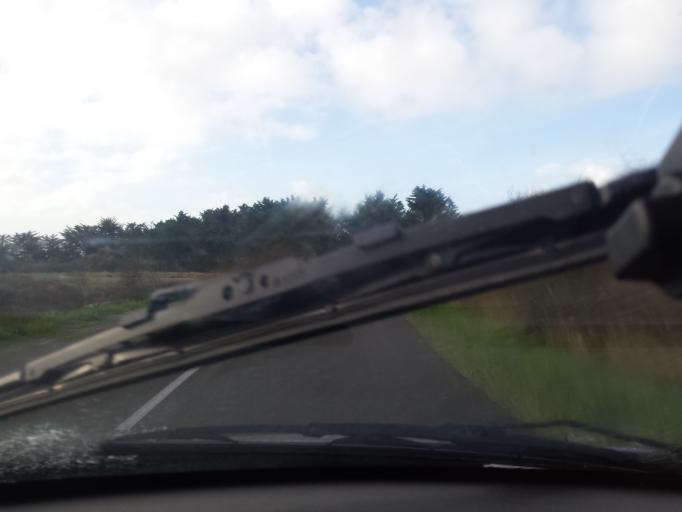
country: FR
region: Pays de la Loire
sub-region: Departement de la Vendee
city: Olonne-sur-Mer
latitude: 46.5518
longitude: -1.7932
